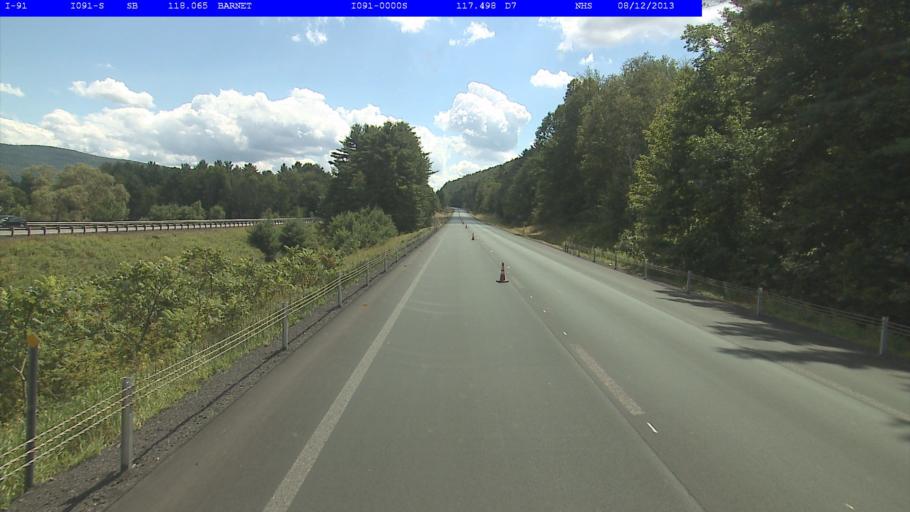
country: US
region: New Hampshire
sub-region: Grafton County
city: Woodsville
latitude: 44.2669
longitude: -72.0703
